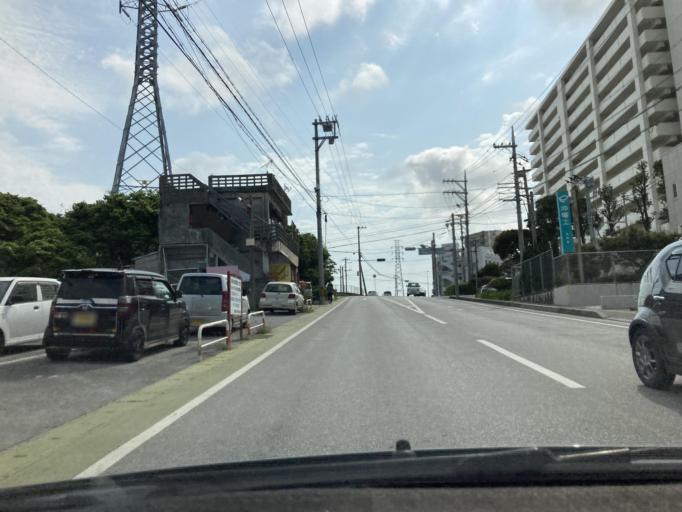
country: JP
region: Okinawa
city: Ginowan
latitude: 26.2688
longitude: 127.7141
